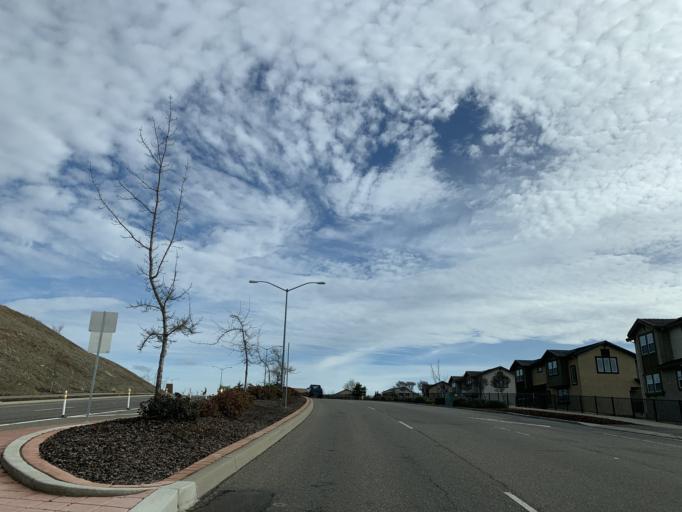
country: US
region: California
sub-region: El Dorado County
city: El Dorado Hills
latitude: 38.6467
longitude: -121.0992
